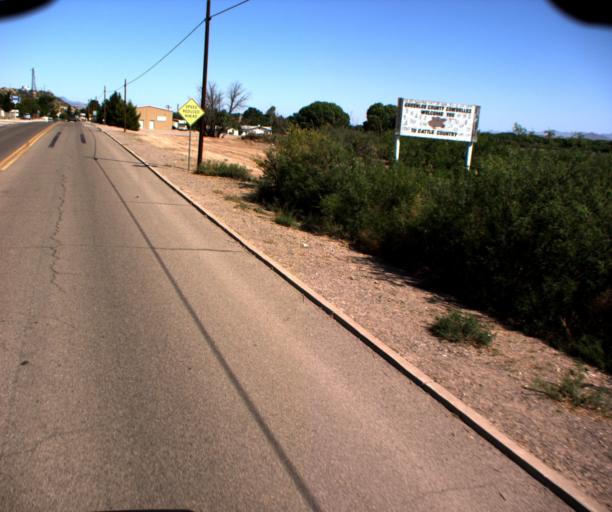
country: US
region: Arizona
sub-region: Greenlee County
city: Clifton
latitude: 32.7119
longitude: -109.0971
